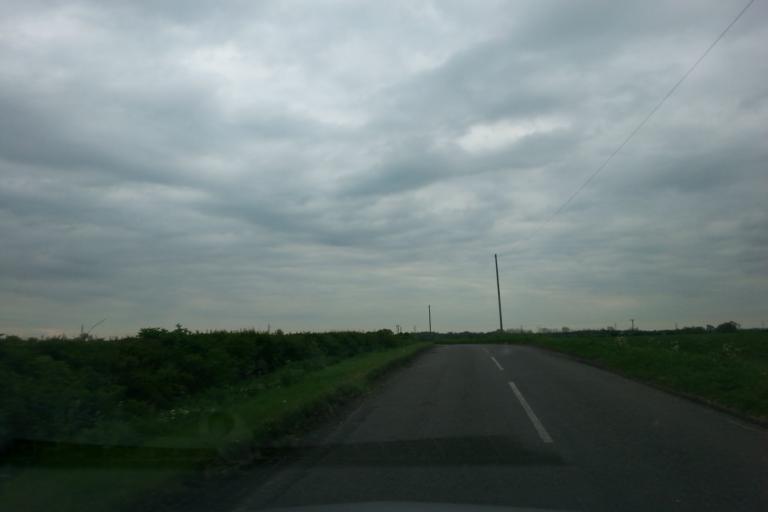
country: GB
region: England
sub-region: Nottinghamshire
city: Farndon
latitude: 53.0090
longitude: -0.8480
